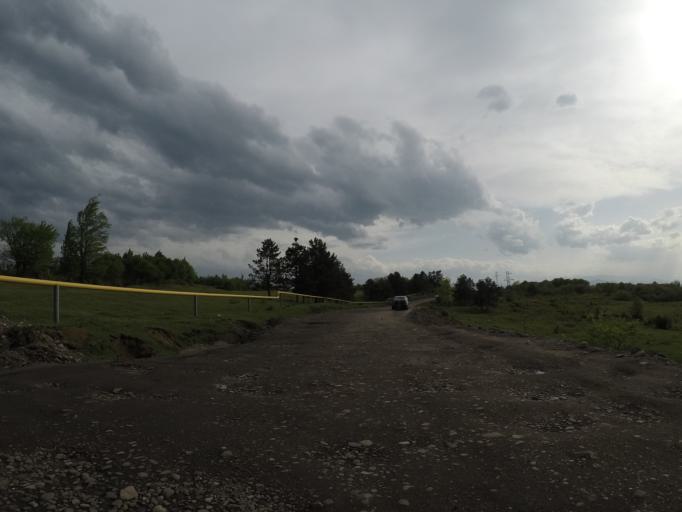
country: GE
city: Shorapani
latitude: 42.1785
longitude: 43.1349
